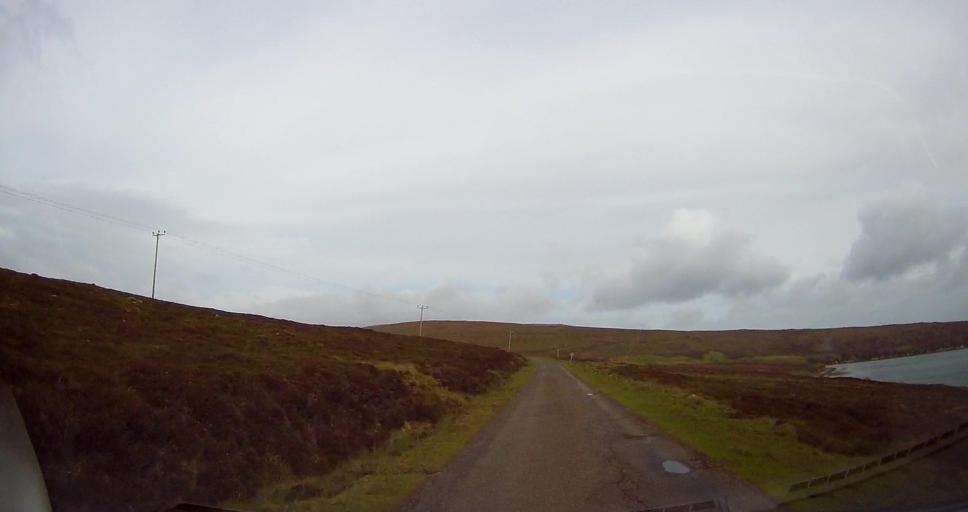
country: GB
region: Scotland
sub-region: Orkney Islands
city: Stromness
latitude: 58.8566
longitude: -3.2142
